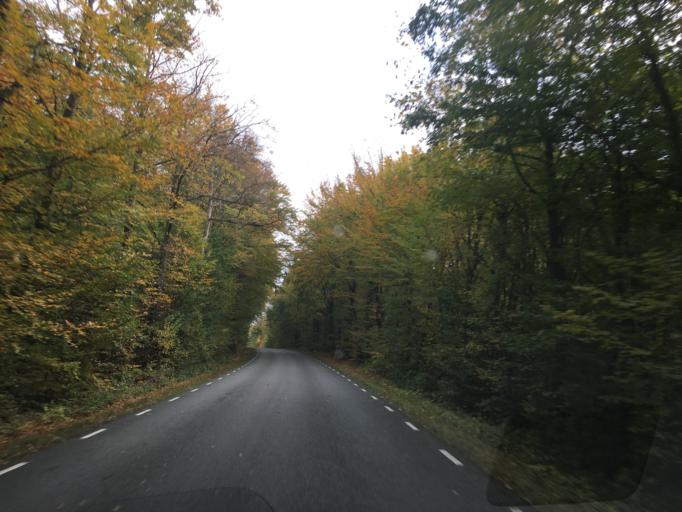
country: SE
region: Skane
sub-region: Tomelilla Kommun
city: Tomelilla
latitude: 55.6408
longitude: 14.0594
